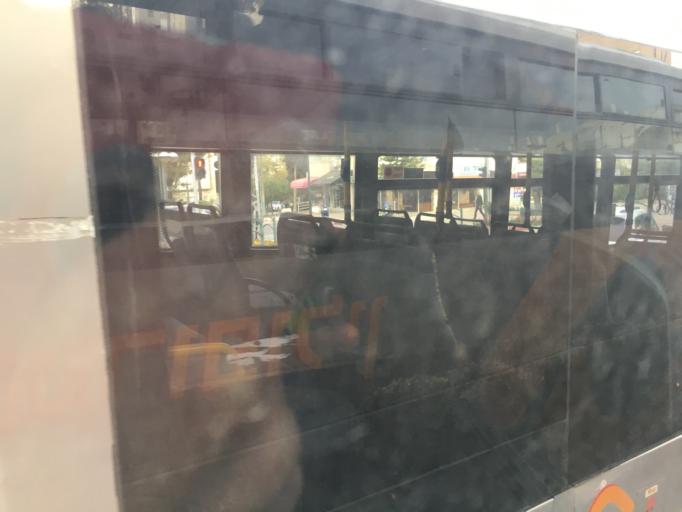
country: IL
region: Central District
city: Kfar Saba
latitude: 32.1759
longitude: 34.9056
